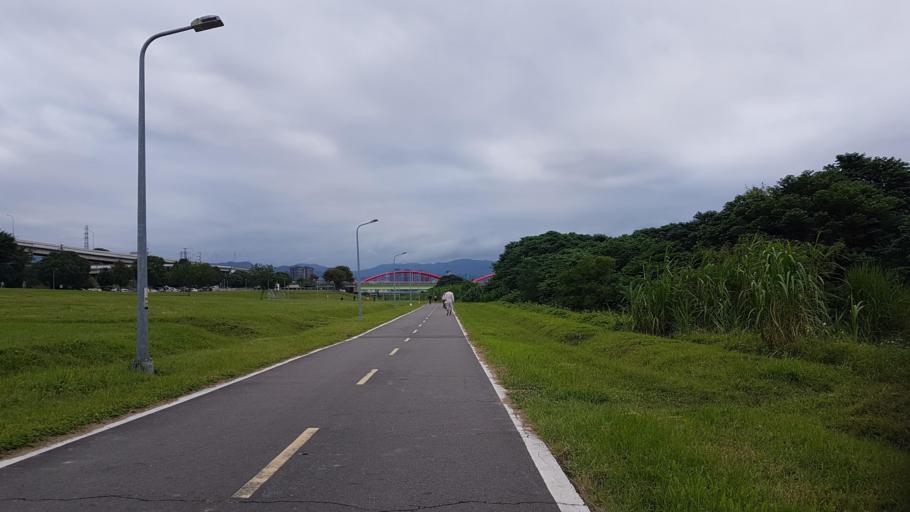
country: TW
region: Taipei
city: Taipei
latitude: 25.0145
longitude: 121.5250
